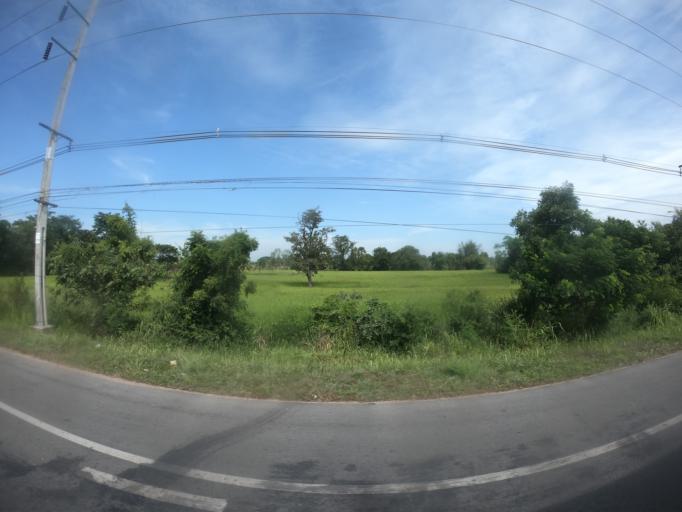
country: TH
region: Maha Sarakham
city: Chiang Yuen
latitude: 16.4448
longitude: 103.0166
